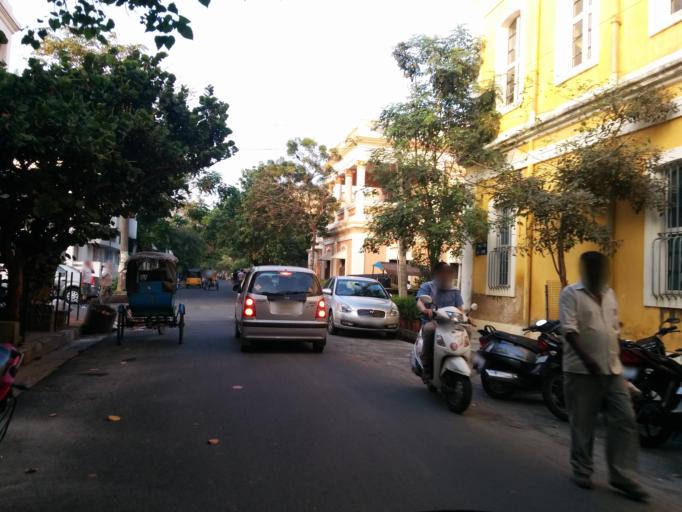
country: IN
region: Pondicherry
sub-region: Puducherry
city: Puducherry
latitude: 11.9272
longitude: 79.8341
